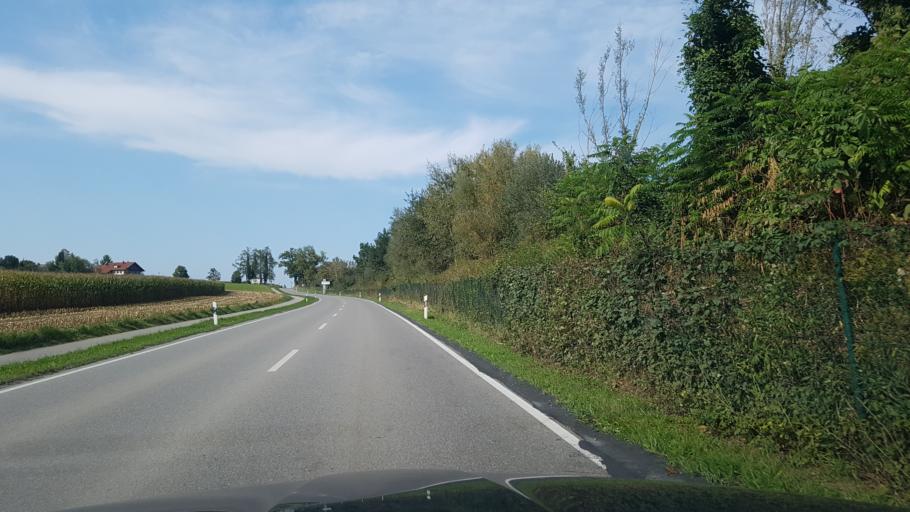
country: DE
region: Bavaria
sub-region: Upper Bavaria
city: Laufen
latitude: 47.8788
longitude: 12.9269
